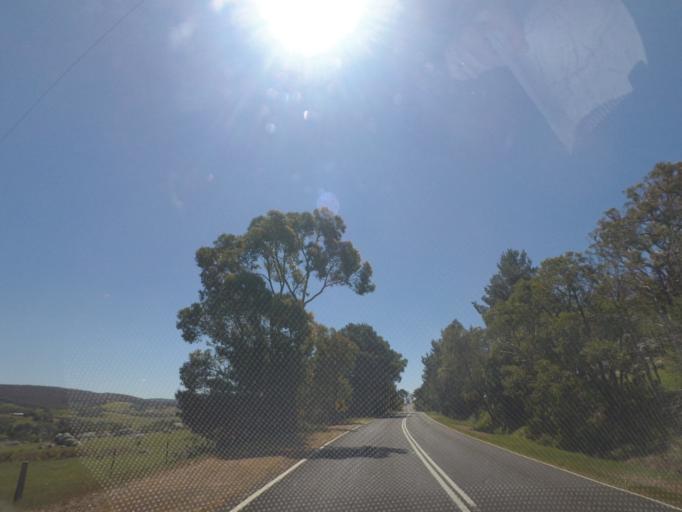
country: AU
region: Victoria
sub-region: Hume
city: Sunbury
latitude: -37.1980
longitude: 144.7386
